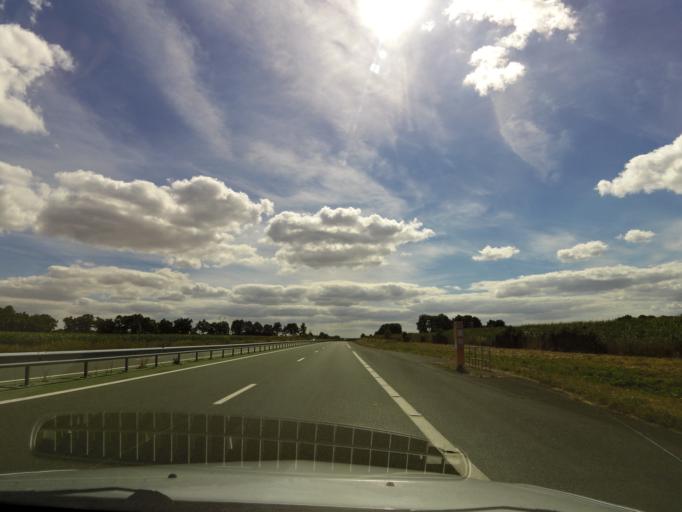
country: FR
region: Pays de la Loire
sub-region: Departement de la Vendee
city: La Ferriere
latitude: 46.7103
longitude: -1.2852
